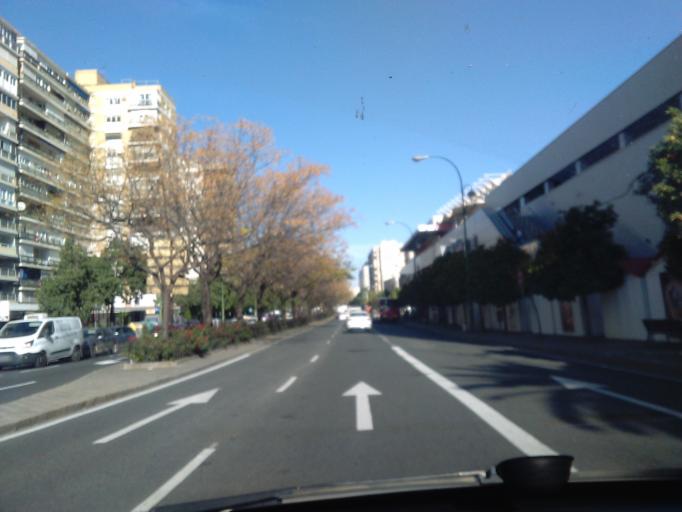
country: ES
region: Andalusia
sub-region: Provincia de Sevilla
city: Sevilla
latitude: 37.3832
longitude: -5.9730
